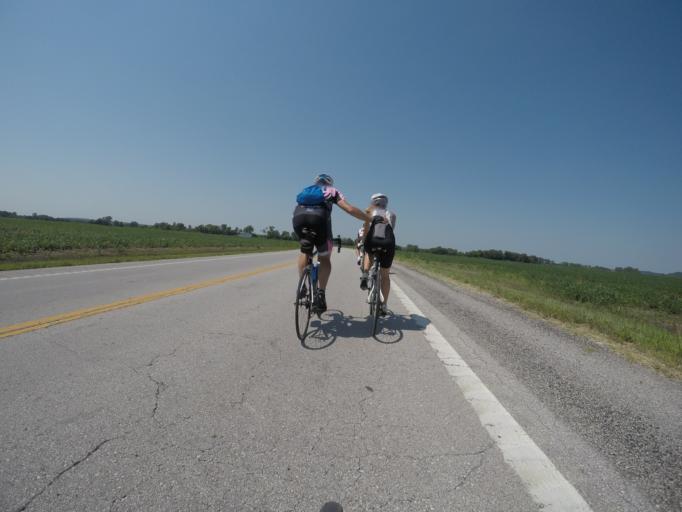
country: US
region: Kansas
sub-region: Leavenworth County
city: Leavenworth
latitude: 39.3235
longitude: -94.8604
